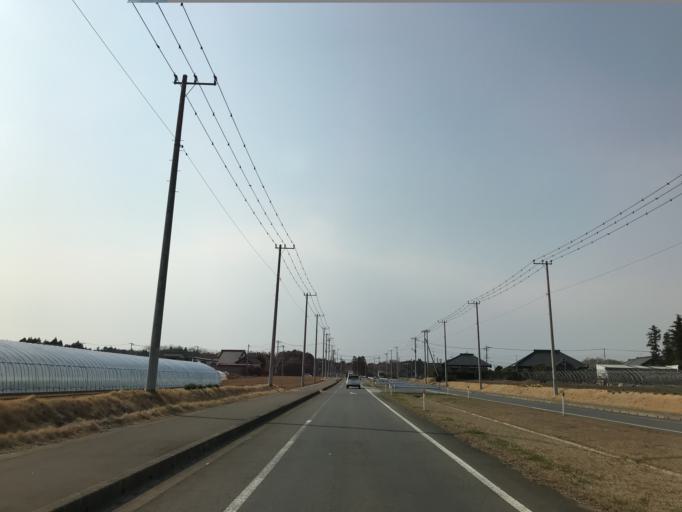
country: JP
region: Ibaraki
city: Okunoya
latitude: 36.1853
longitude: 140.3924
